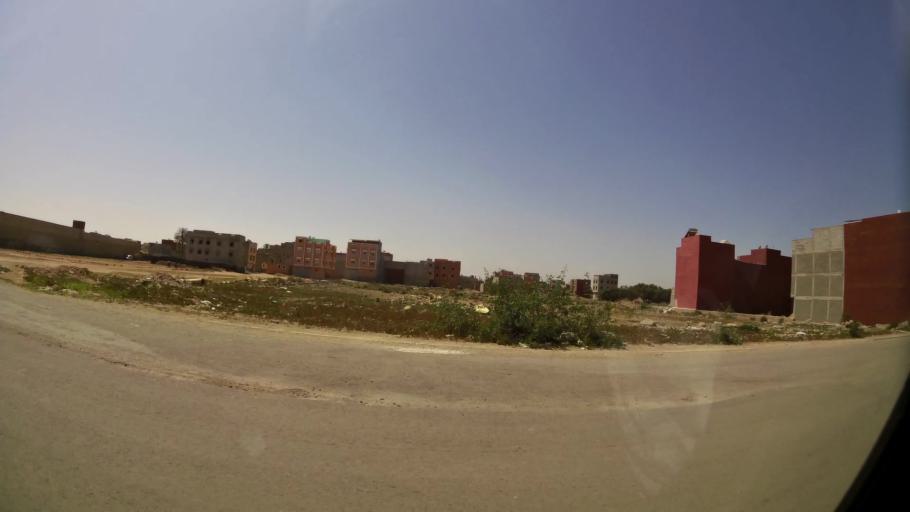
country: MA
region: Souss-Massa-Draa
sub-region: Inezgane-Ait Mellou
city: Inezgane
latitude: 30.3174
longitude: -9.5069
